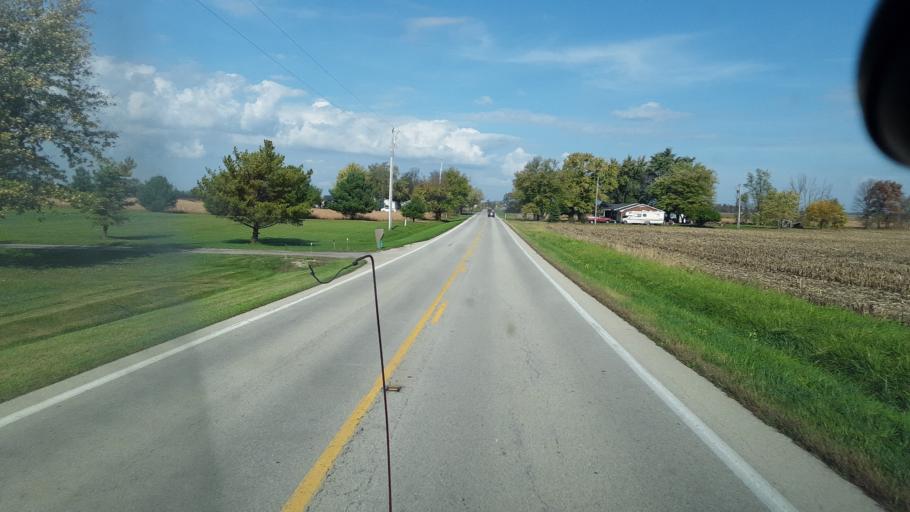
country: US
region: Ohio
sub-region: Clinton County
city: Sabina
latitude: 39.5439
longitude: -83.7106
